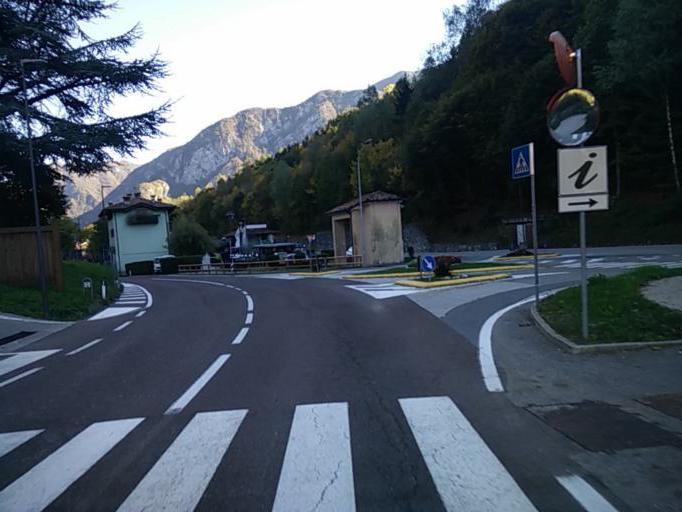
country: IT
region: Trentino-Alto Adige
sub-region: Provincia di Trento
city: Molina di Ledro
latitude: 45.8737
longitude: 10.7667
